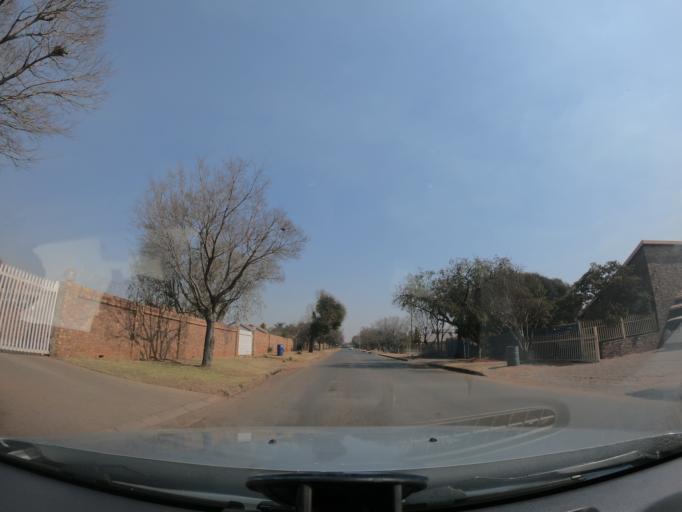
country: ZA
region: Mpumalanga
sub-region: Nkangala District Municipality
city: Middelburg
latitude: -25.7972
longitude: 29.4610
